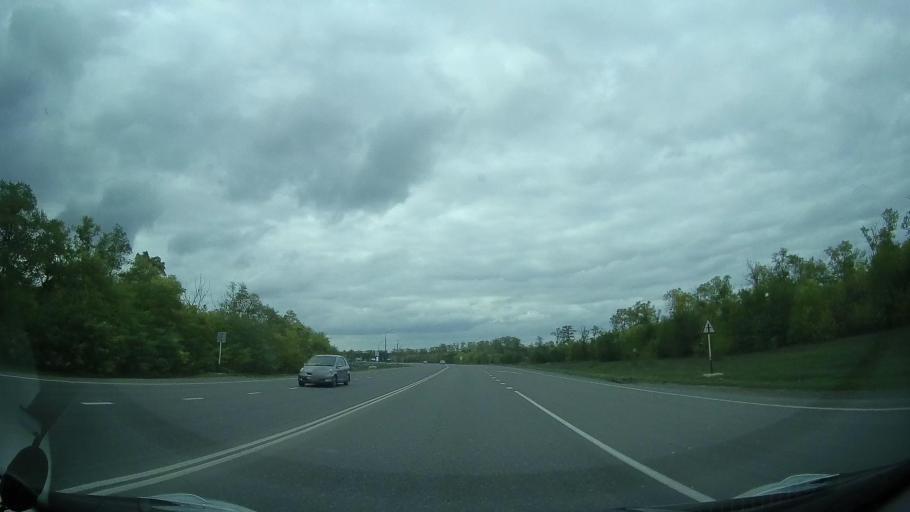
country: RU
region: Rostov
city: Mechetinskaya
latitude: 46.7539
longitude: 40.4584
